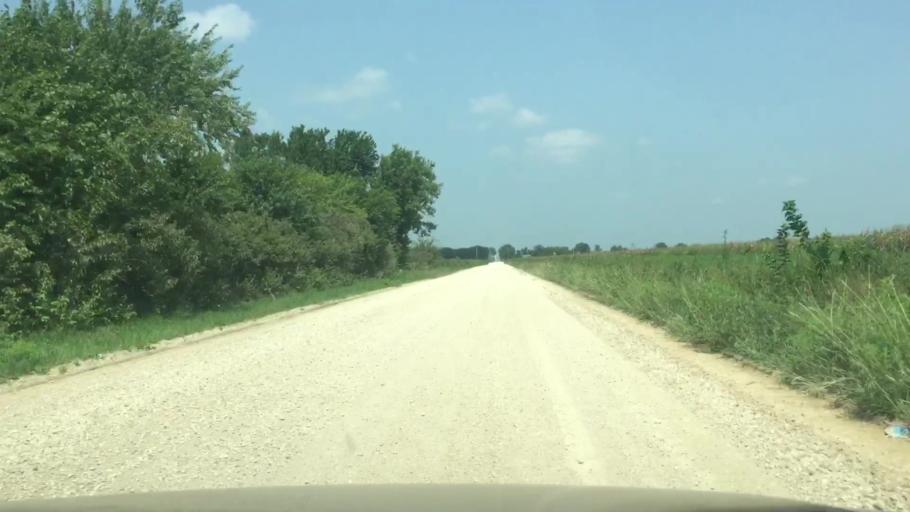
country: US
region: Kansas
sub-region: Allen County
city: Iola
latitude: 37.8705
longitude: -95.3911
